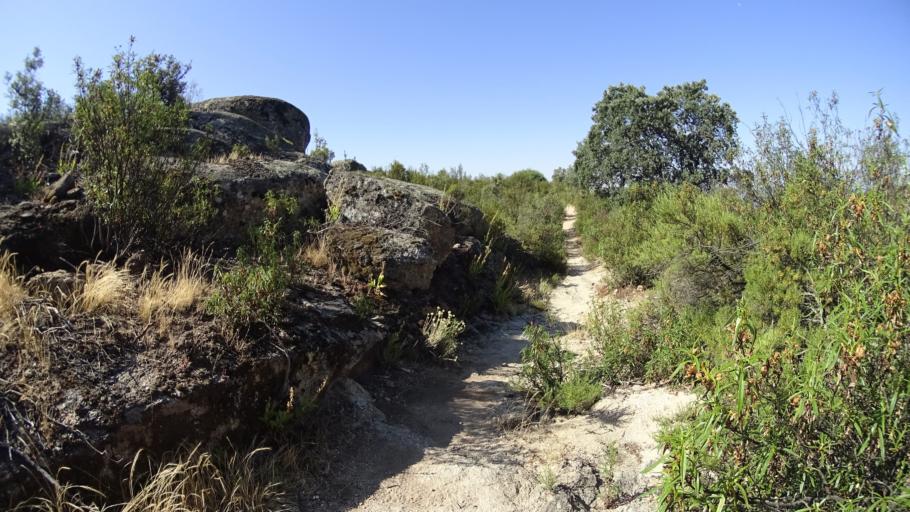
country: ES
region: Madrid
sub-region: Provincia de Madrid
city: Hoyo de Manzanares
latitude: 40.6421
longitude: -3.9362
